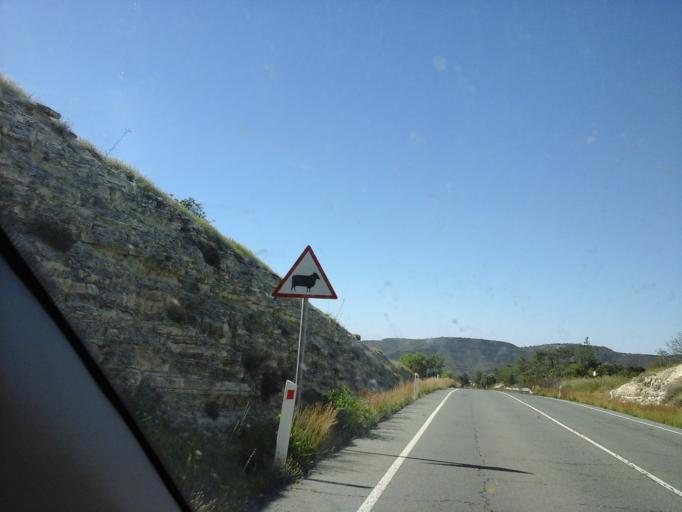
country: CY
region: Limassol
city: Sotira
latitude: 34.7842
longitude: 32.9159
